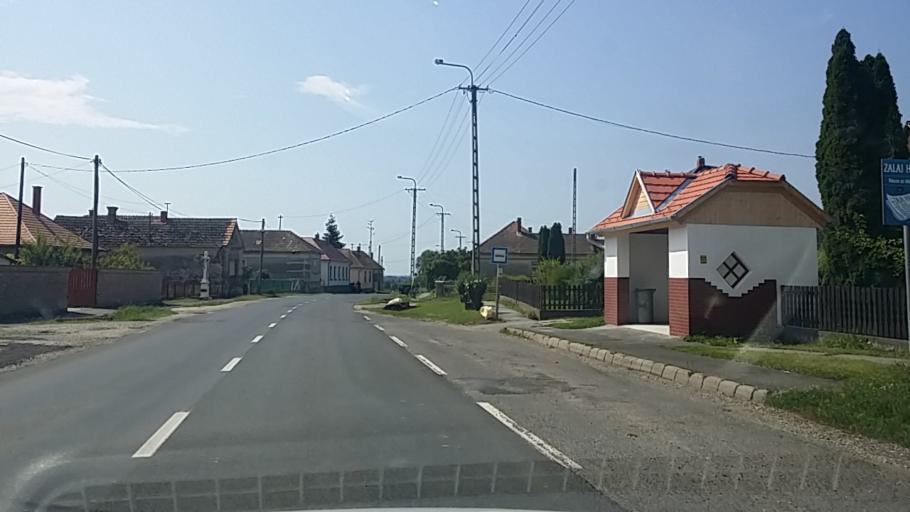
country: HU
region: Zala
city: Lenti
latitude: 46.5642
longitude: 16.5565
